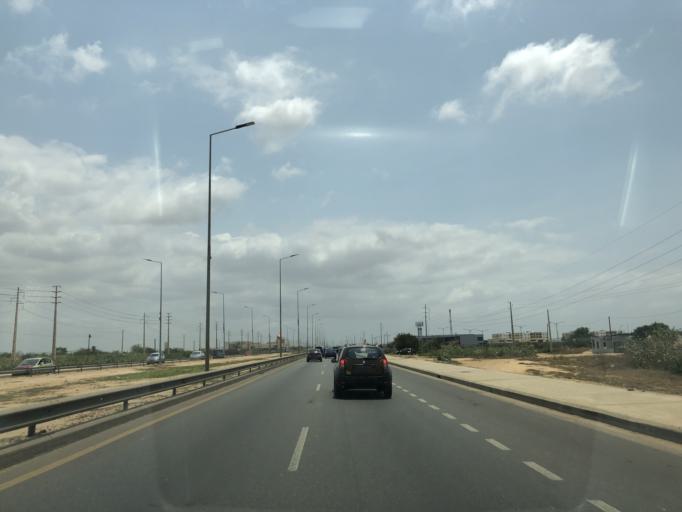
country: AO
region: Luanda
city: Luanda
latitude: -8.9503
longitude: 13.2593
